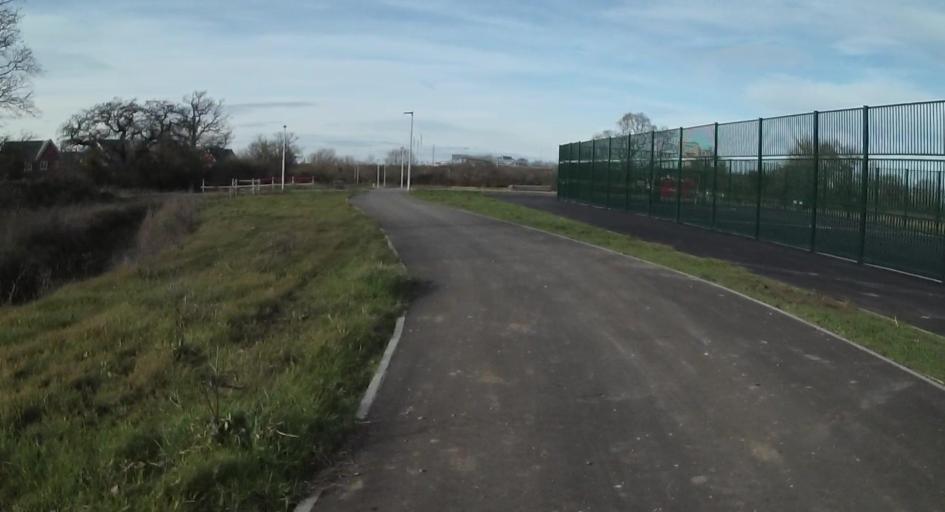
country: GB
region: England
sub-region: Wokingham
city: Shinfield
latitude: 51.4082
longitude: -0.9701
